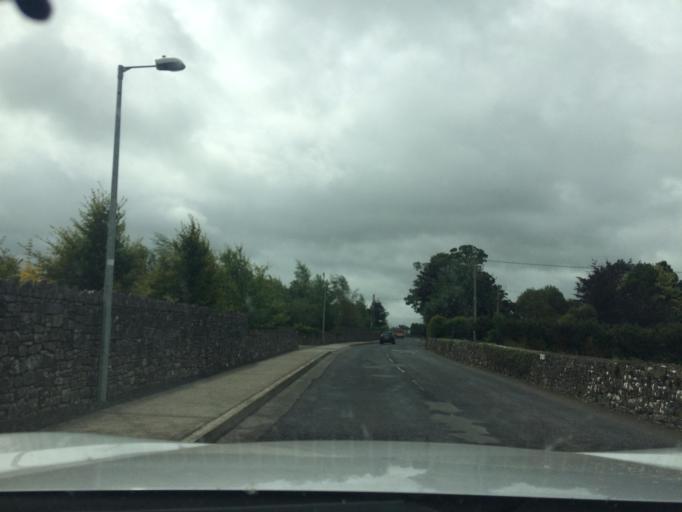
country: IE
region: Munster
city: Thurles
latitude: 52.6361
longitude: -7.8678
